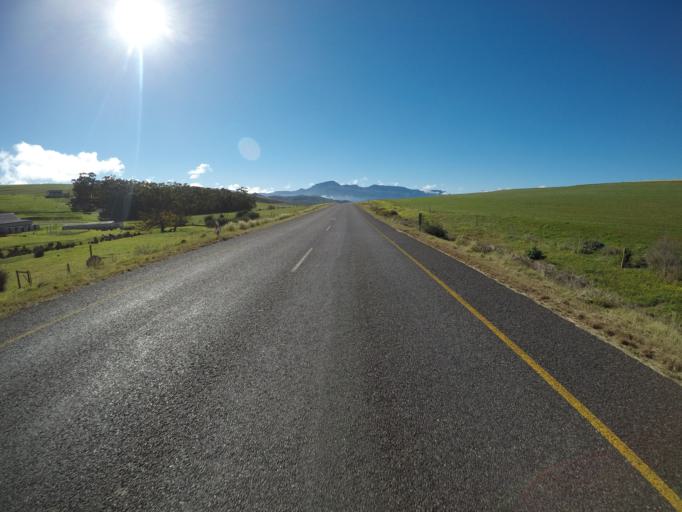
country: ZA
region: Western Cape
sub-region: Overberg District Municipality
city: Caledon
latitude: -34.1233
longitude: 19.5156
